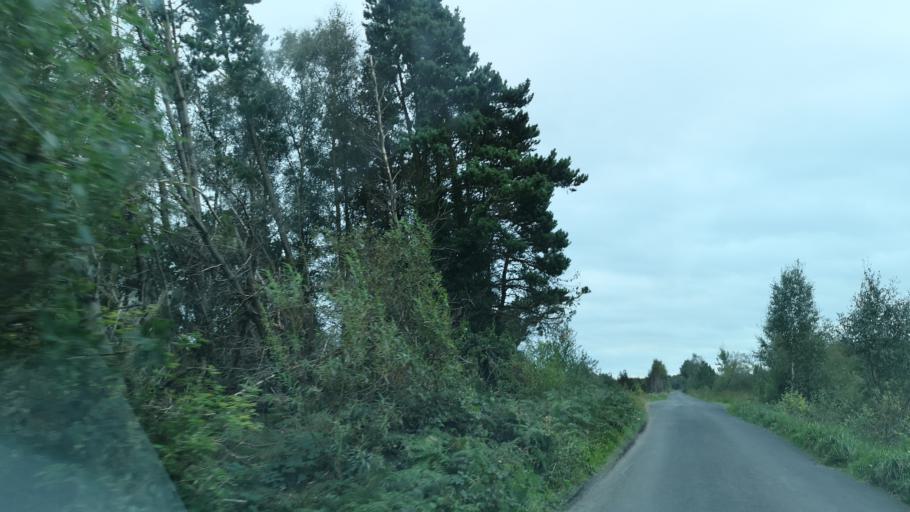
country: IE
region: Leinster
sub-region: Uibh Fhaili
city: Ferbane
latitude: 53.2083
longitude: -7.7236
